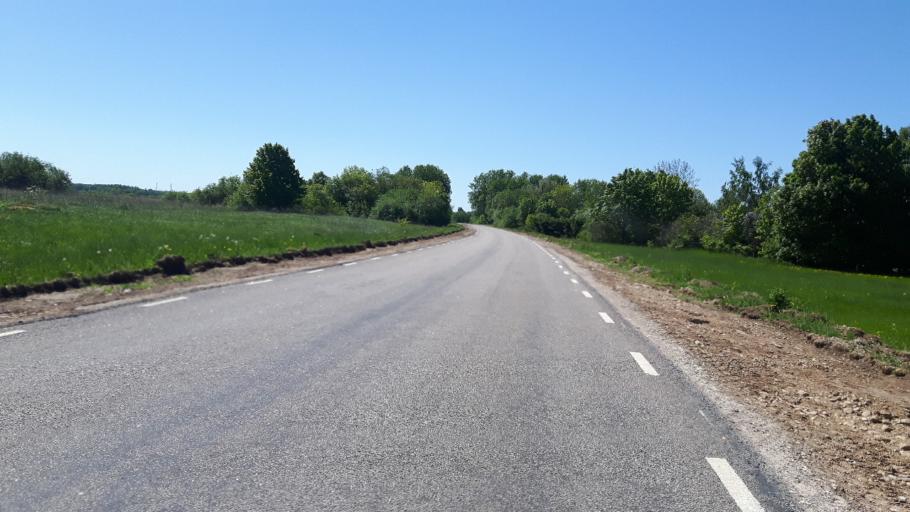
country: EE
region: Ida-Virumaa
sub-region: Narva-Joesuu linn
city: Narva-Joesuu
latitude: 59.3939
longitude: 27.9248
